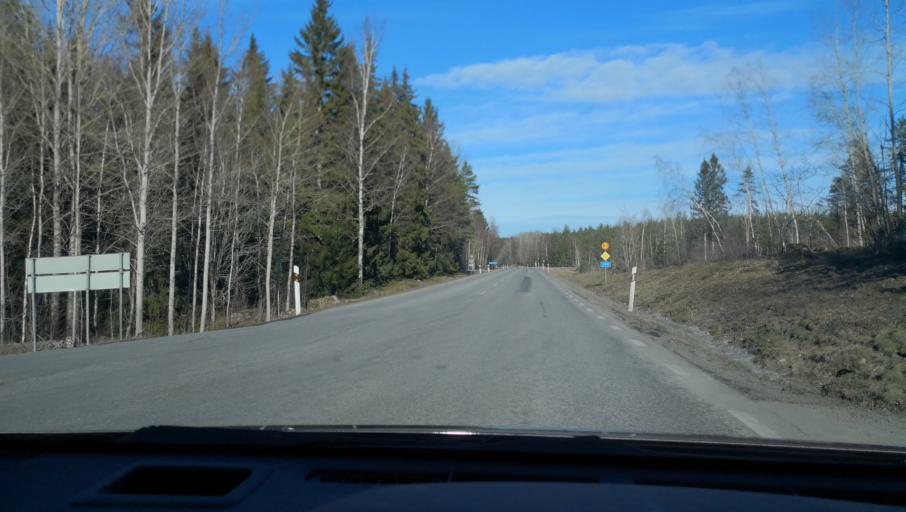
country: SE
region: Uppsala
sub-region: Uppsala Kommun
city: Vattholma
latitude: 60.0227
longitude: 17.7470
